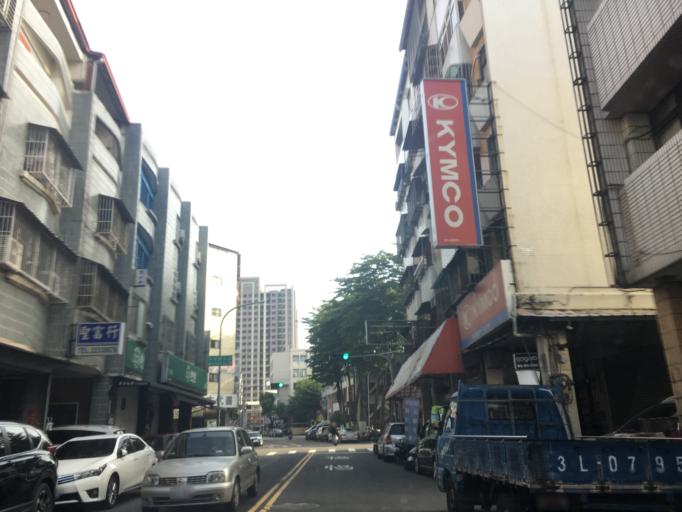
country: TW
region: Taiwan
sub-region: Taichung City
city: Taichung
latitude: 24.1693
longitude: 120.6803
